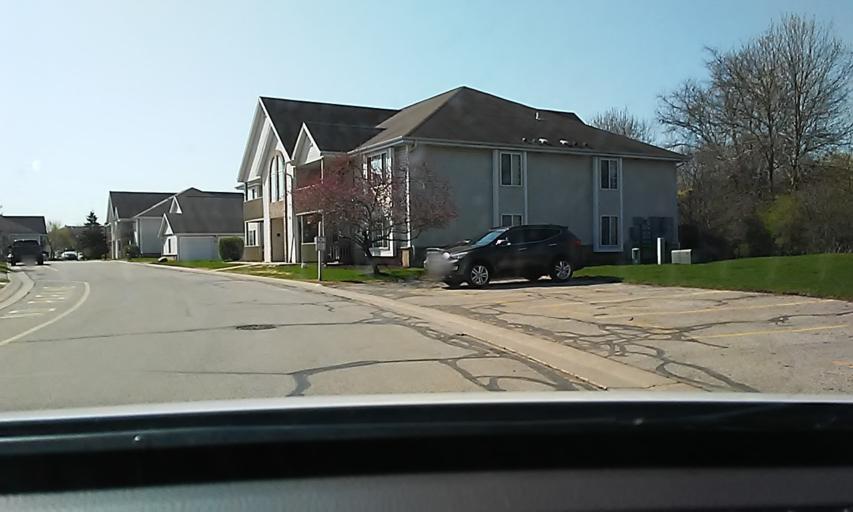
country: US
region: Wisconsin
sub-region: Milwaukee County
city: Hales Corners
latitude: 42.9800
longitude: -88.0533
